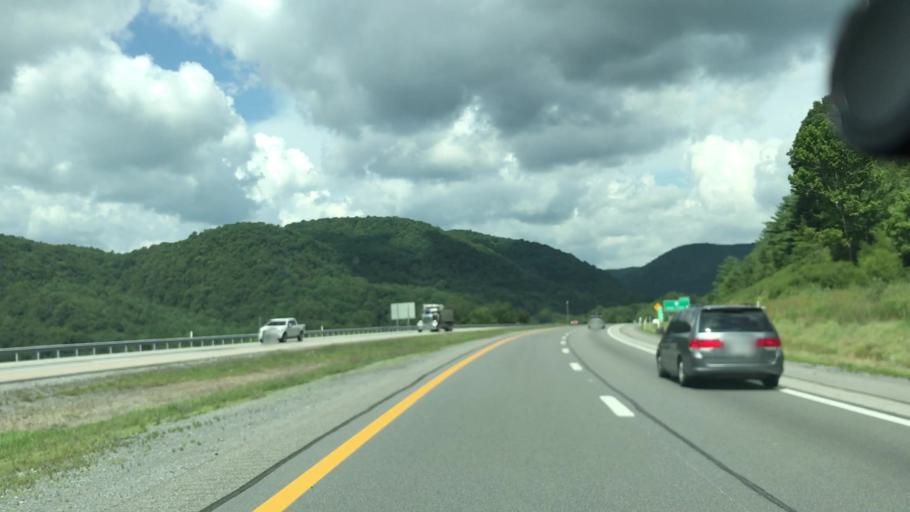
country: US
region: West Virginia
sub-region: Mercer County
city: Athens
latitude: 37.4940
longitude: -81.0984
